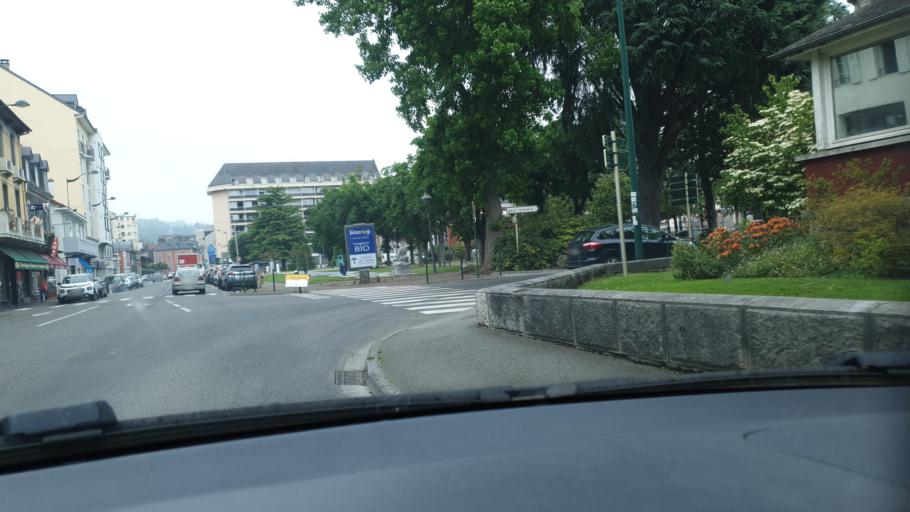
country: FR
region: Midi-Pyrenees
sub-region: Departement des Hautes-Pyrenees
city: Lourdes
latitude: 43.0920
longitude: -0.0462
